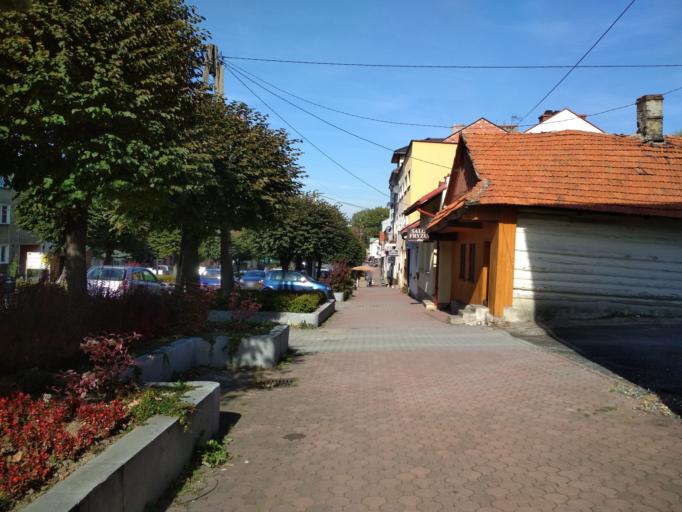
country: PL
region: Lesser Poland Voivodeship
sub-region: Powiat wadowicki
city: Kalwaria Zebrzydowska
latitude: 49.8643
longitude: 19.6760
